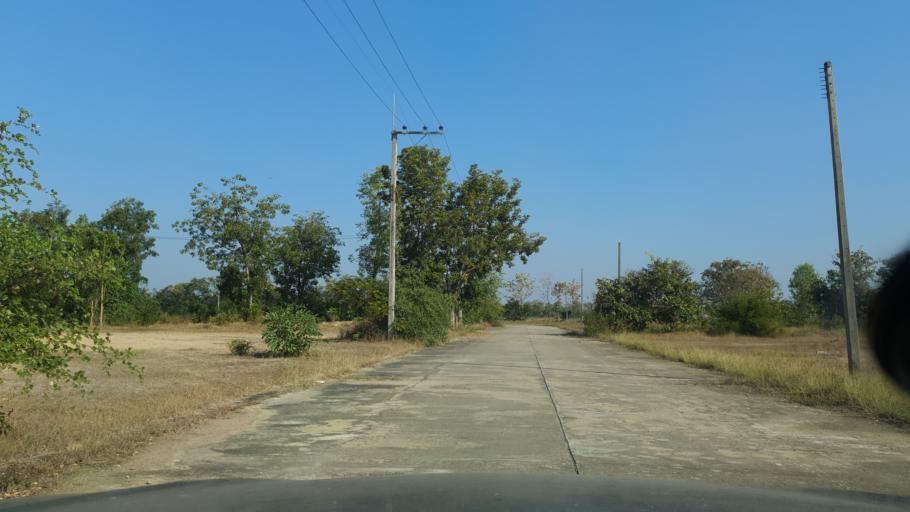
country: TH
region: Lamphun
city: Ban Thi
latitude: 18.6720
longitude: 99.1249
